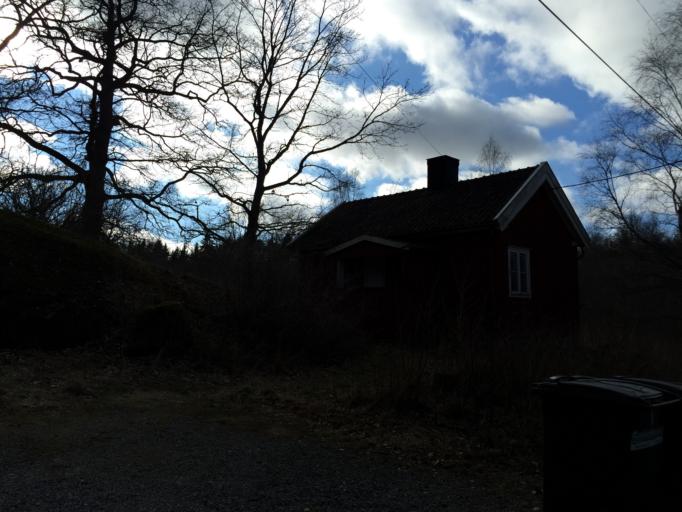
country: SE
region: Stockholm
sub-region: Salems Kommun
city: Ronninge
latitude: 59.1868
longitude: 17.7160
